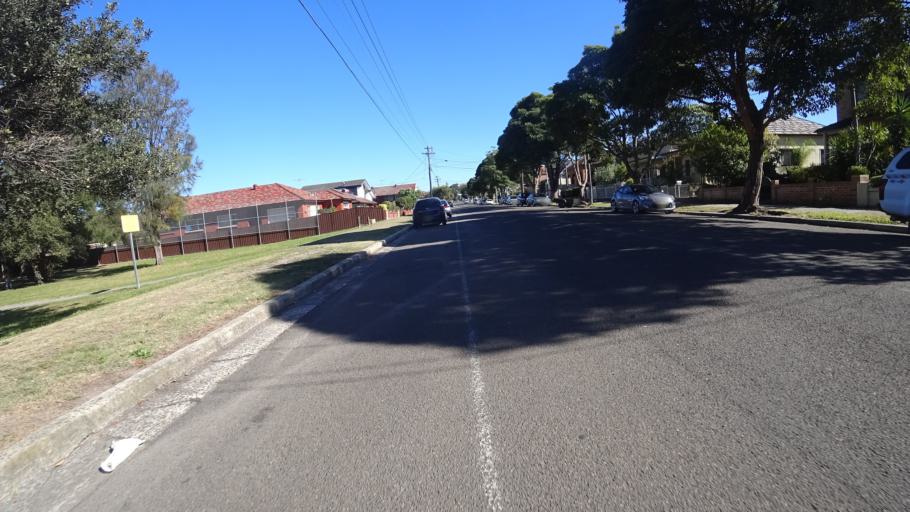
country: AU
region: New South Wales
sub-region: Rockdale
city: Banksia
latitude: -33.9444
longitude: 151.1467
